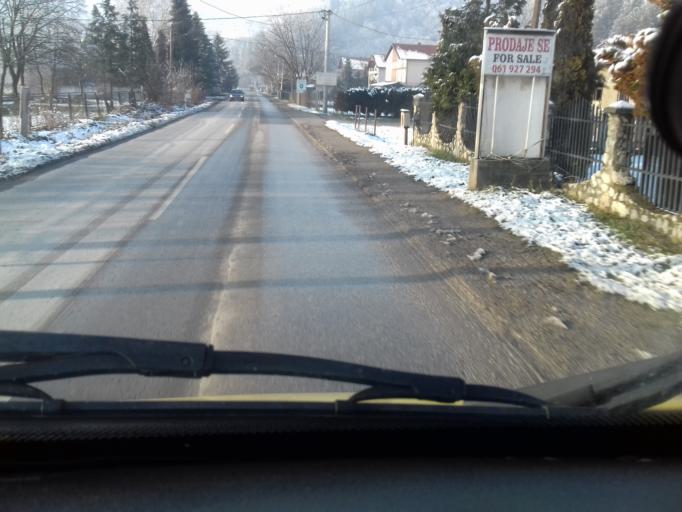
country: BA
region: Federation of Bosnia and Herzegovina
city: Mahala
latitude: 43.9955
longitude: 18.2201
